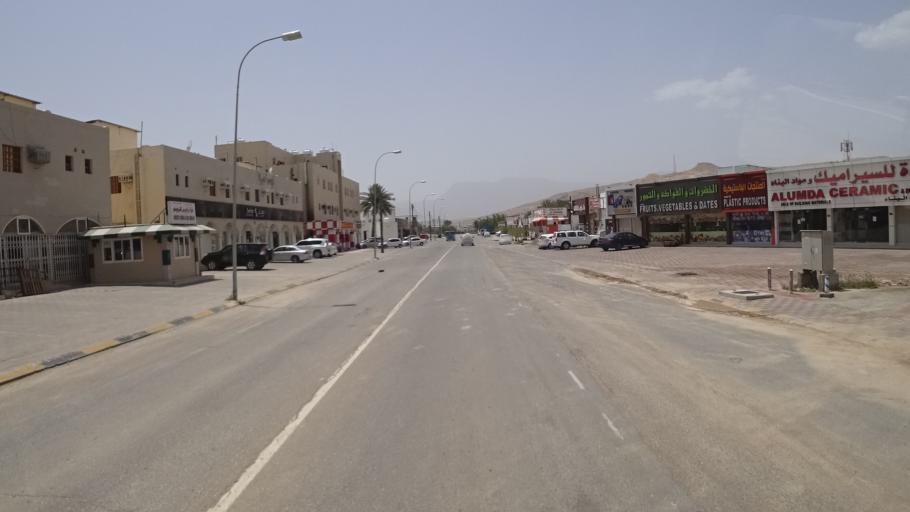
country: OM
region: Muhafazat Masqat
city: Muscat
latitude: 23.2415
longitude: 58.9027
